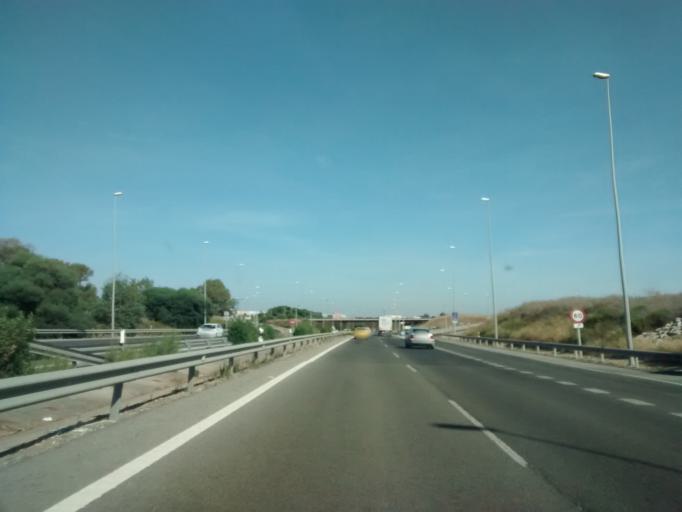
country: ES
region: Andalusia
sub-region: Provincia de Cadiz
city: Chiclana de la Frontera
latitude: 36.3942
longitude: -6.1225
